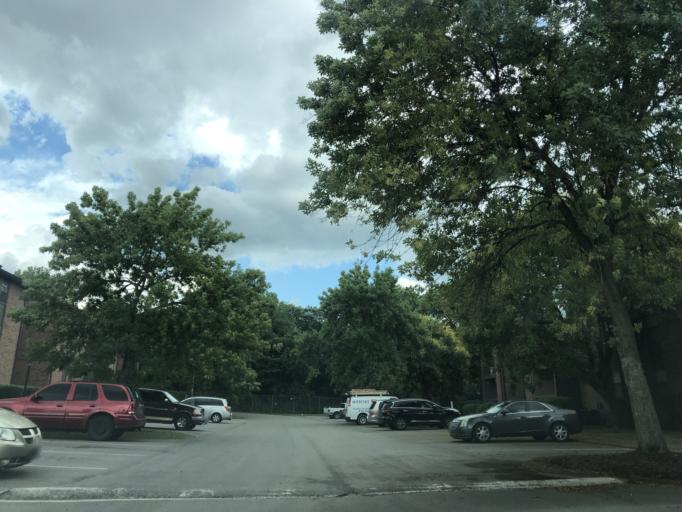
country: US
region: Tennessee
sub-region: Davidson County
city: Nashville
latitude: 36.2232
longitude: -86.7641
